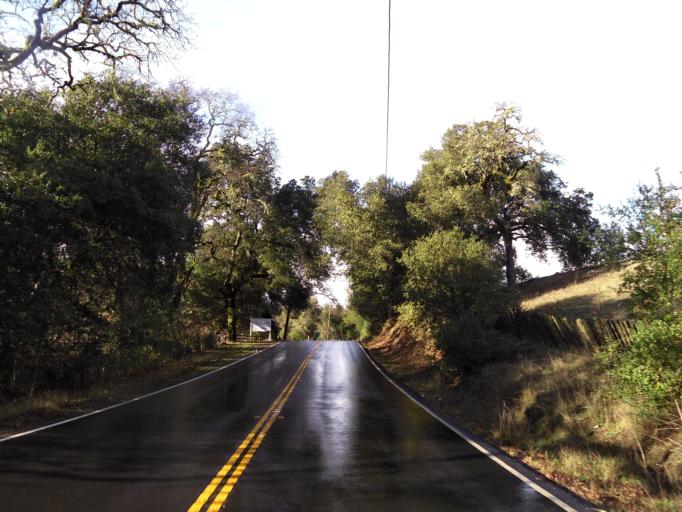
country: US
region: California
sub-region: Sonoma County
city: Cloverdale
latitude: 38.8780
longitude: -123.1116
